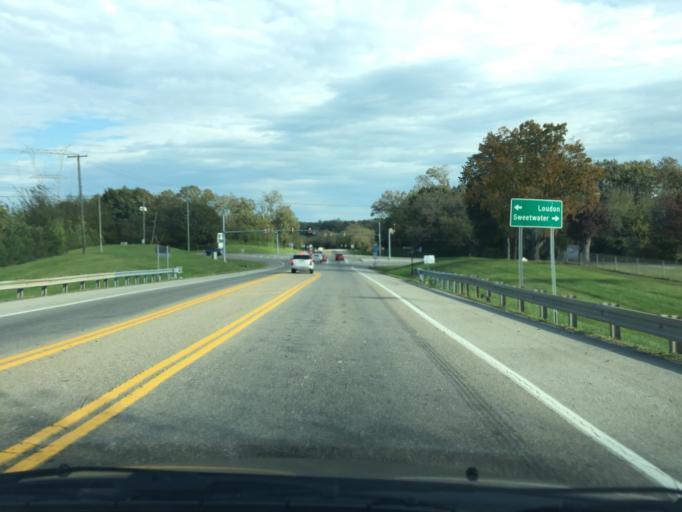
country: US
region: Tennessee
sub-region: Loudon County
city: Loudon
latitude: 35.7187
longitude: -84.3601
